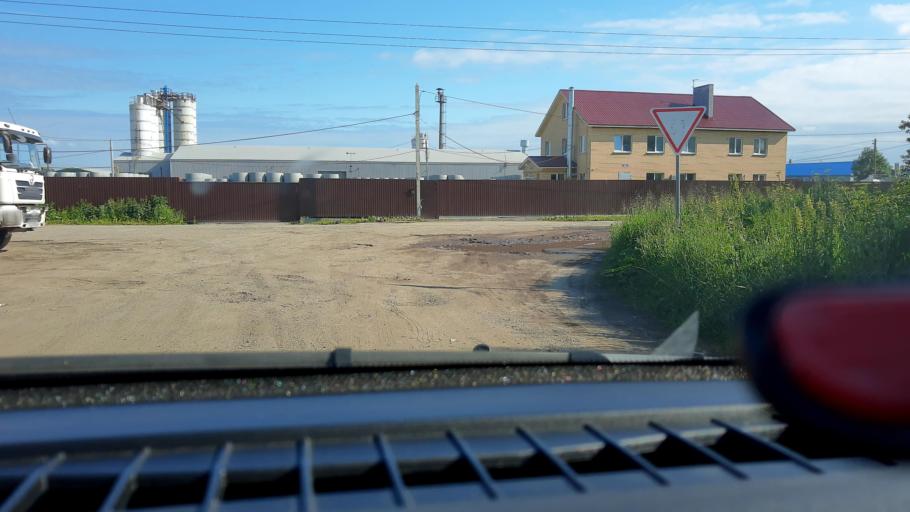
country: RU
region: Nizjnij Novgorod
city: Kstovo
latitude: 56.1972
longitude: 44.1528
